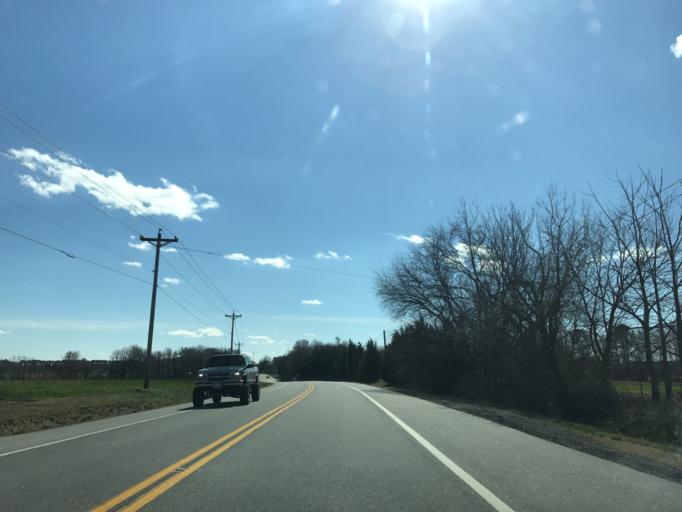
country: US
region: Maryland
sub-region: Kent County
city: Rock Hall
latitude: 39.1613
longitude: -76.2046
